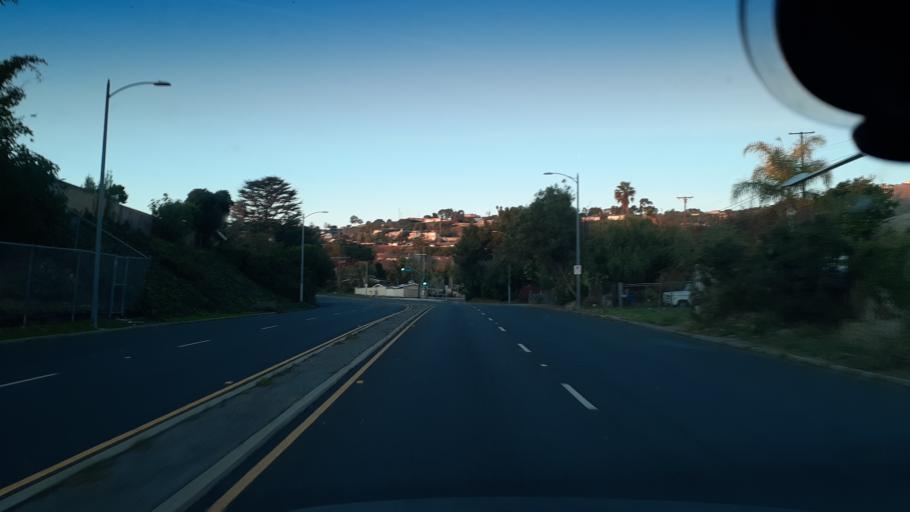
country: US
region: California
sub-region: Los Angeles County
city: San Pedro
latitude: 33.7388
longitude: -118.3136
